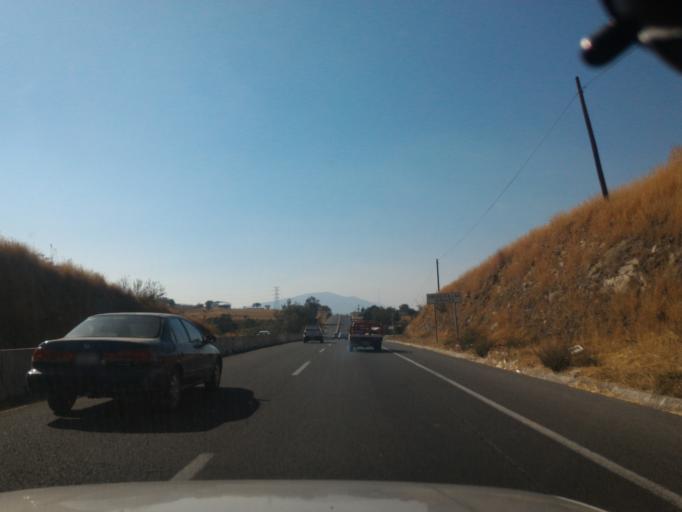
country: MX
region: Jalisco
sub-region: Poncitlan
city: Cuitzeo (La Estancia)
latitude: 20.3653
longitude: -102.8209
